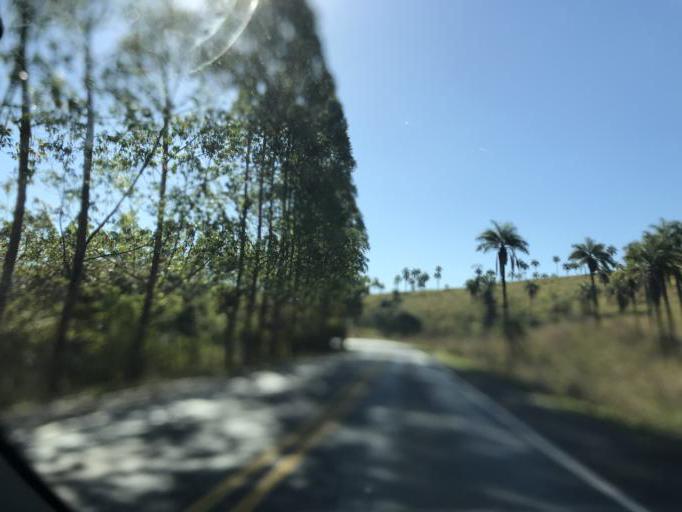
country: BR
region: Minas Gerais
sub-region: Bambui
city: Bambui
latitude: -19.8196
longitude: -46.0198
